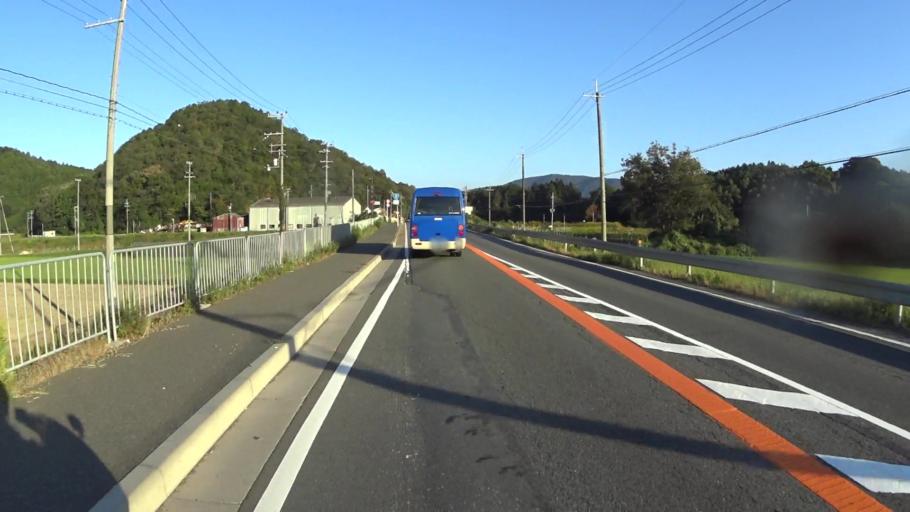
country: JP
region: Kyoto
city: Ayabe
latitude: 35.1765
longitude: 135.4053
